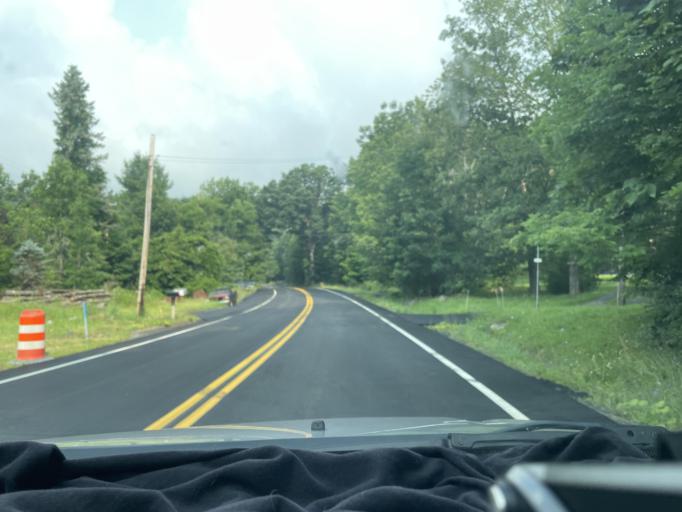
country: US
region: Maryland
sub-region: Garrett County
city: Mountain Lake Park
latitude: 39.3013
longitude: -79.3925
